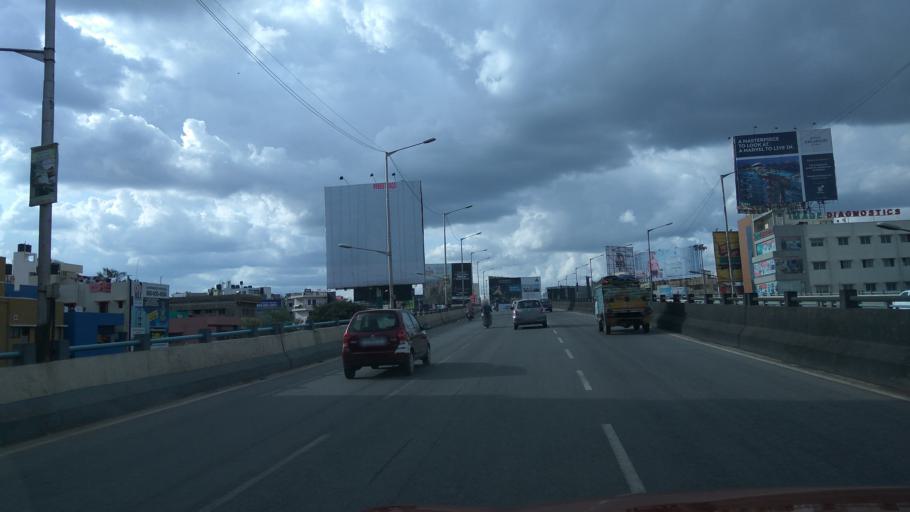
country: IN
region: Karnataka
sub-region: Bangalore Urban
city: Yelahanka
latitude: 13.0389
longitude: 77.6252
